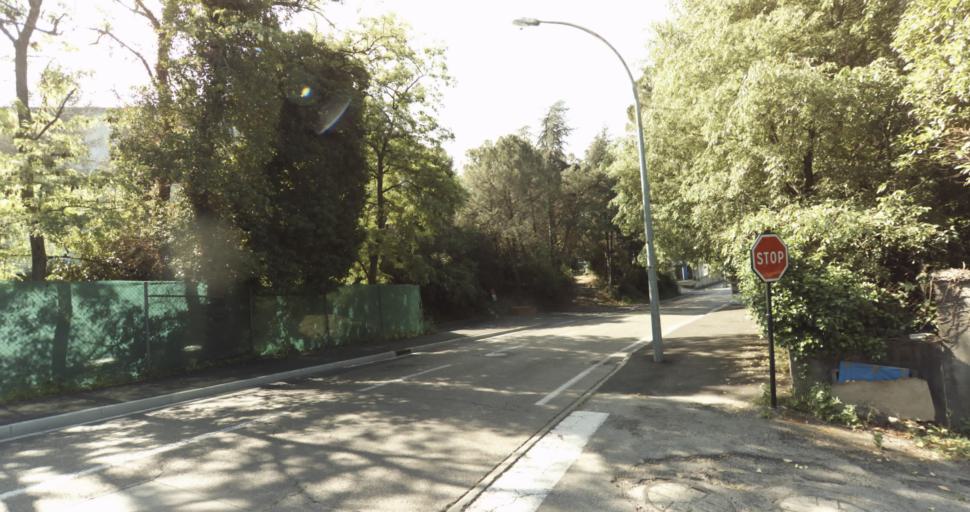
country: FR
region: Languedoc-Roussillon
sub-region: Departement du Gard
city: Nimes
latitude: 43.8320
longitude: 4.3240
